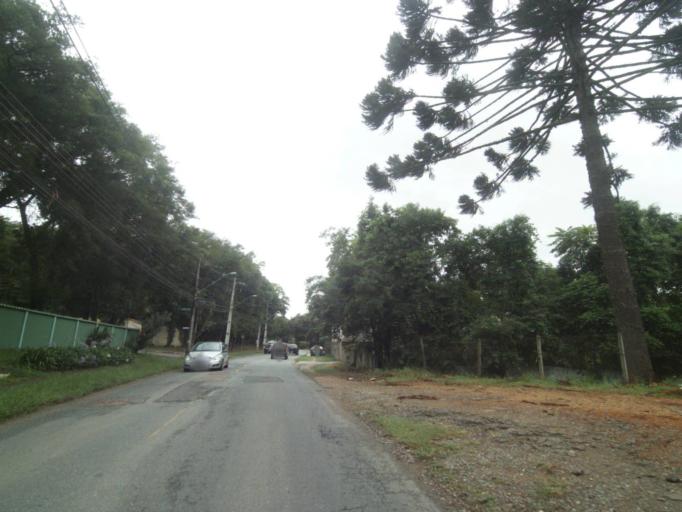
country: BR
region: Parana
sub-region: Curitiba
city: Curitiba
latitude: -25.4444
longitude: -49.3217
